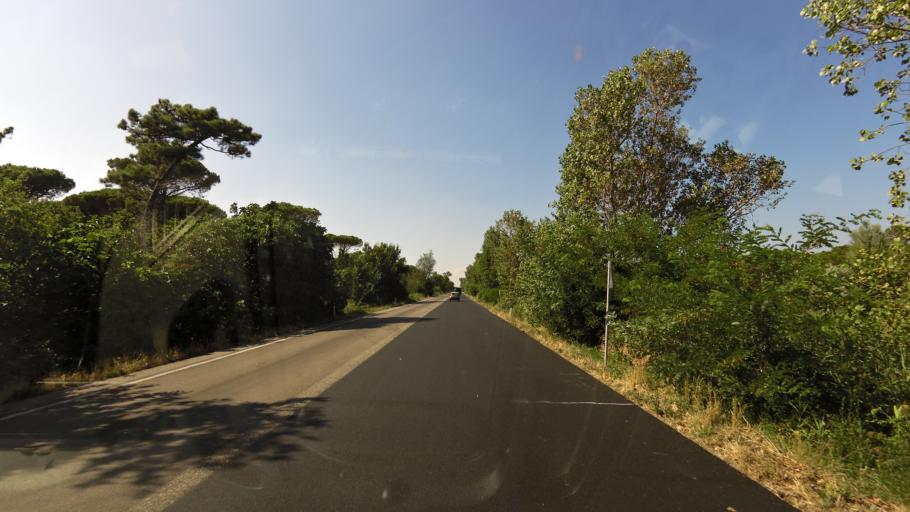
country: IT
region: Emilia-Romagna
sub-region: Provincia di Ferrara
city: Lido degli Estensi
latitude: 44.5952
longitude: 12.2489
